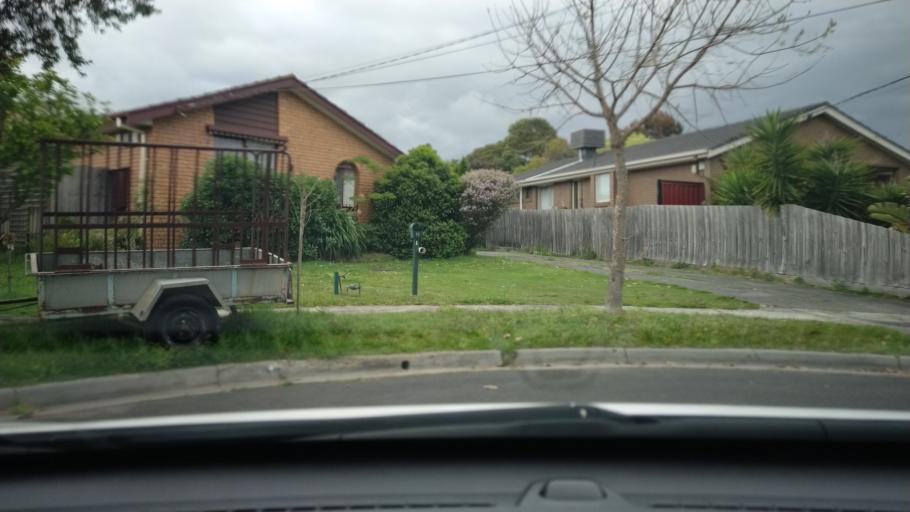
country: AU
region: Victoria
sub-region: Greater Dandenong
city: Springvale South
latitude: -37.9797
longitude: 145.1572
